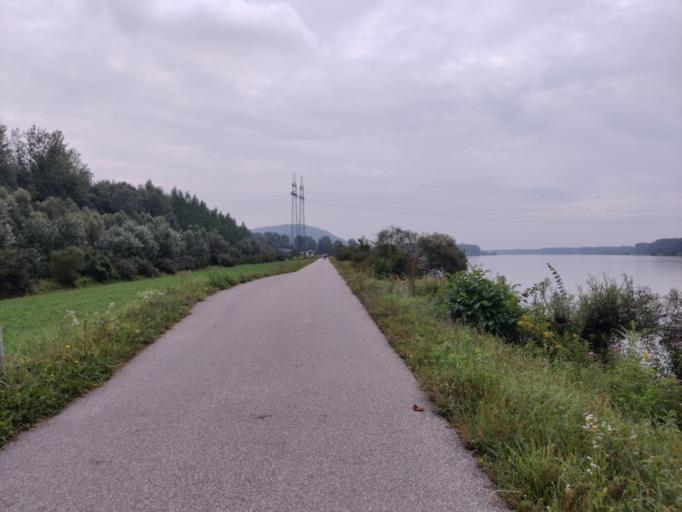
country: AT
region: Upper Austria
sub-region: Politischer Bezirk Urfahr-Umgebung
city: Steyregg
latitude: 48.2715
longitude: 14.3773
